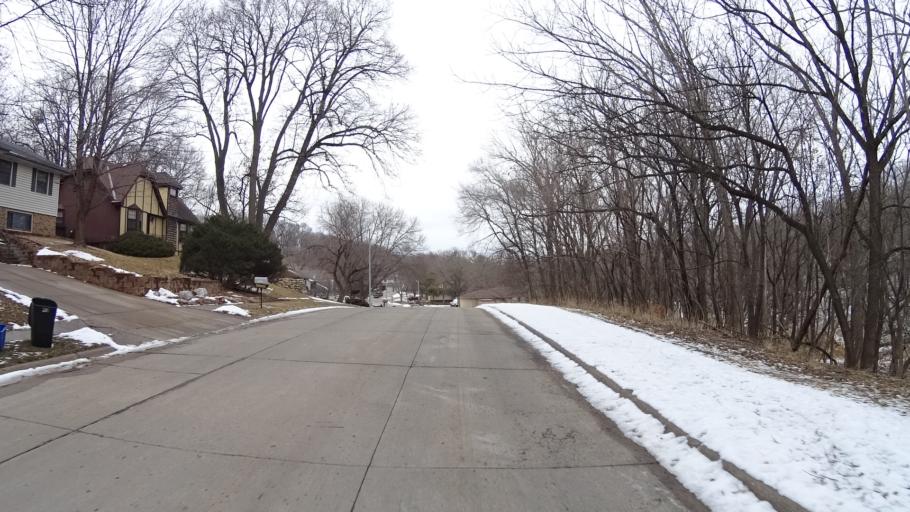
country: US
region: Nebraska
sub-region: Sarpy County
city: Bellevue
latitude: 41.1736
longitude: -95.9158
